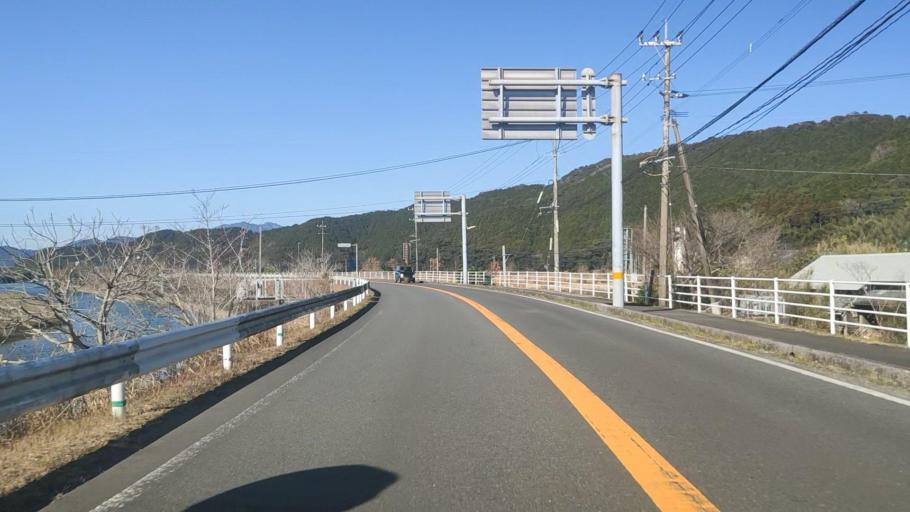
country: JP
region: Oita
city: Saiki
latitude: 32.9340
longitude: 131.9215
